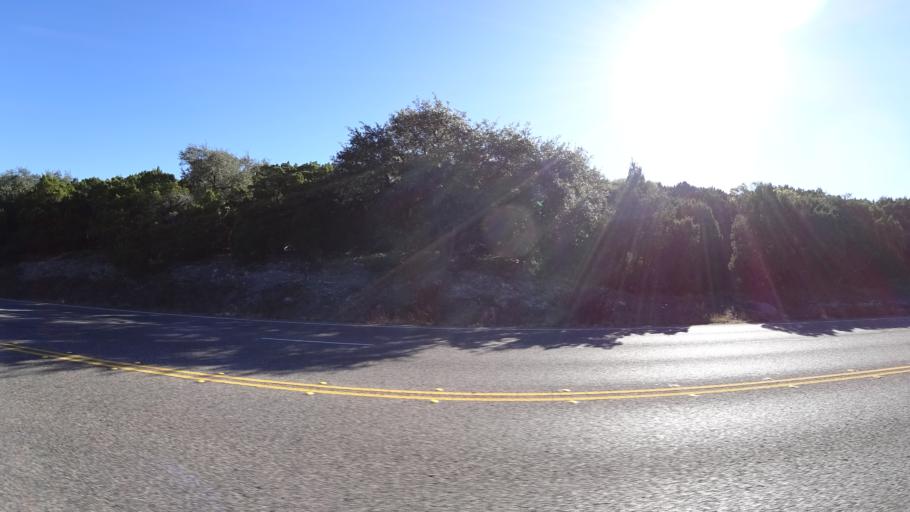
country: US
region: Texas
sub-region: Travis County
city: West Lake Hills
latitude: 30.3496
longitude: -97.7855
